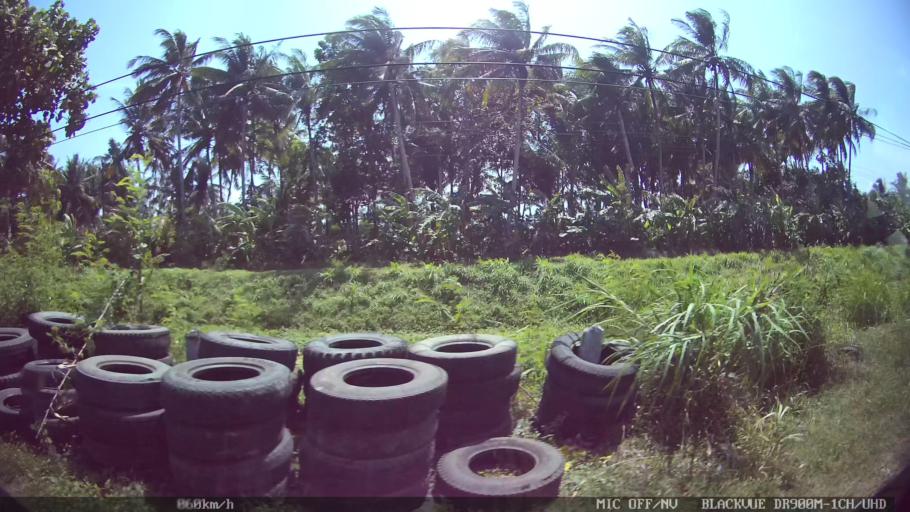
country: ID
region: Daerah Istimewa Yogyakarta
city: Srandakan
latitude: -7.9388
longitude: 110.1578
